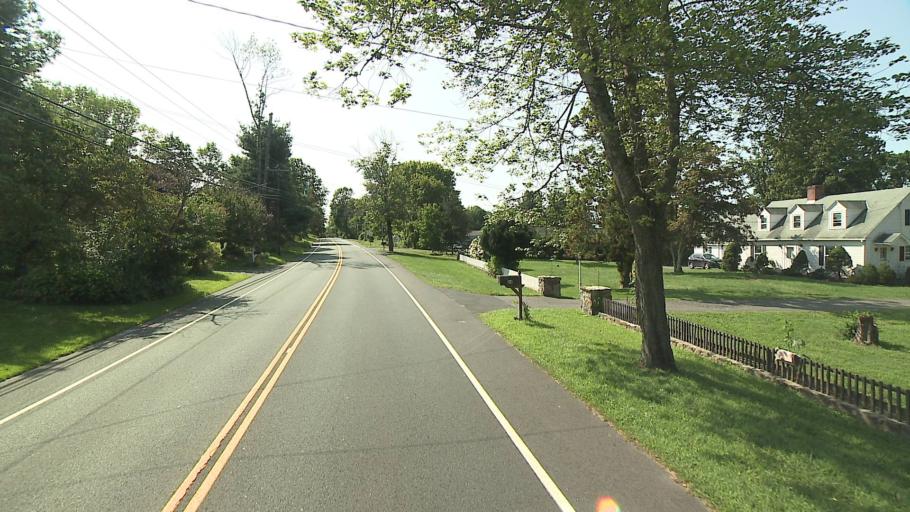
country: US
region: Connecticut
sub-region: Fairfield County
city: Newtown
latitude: 41.4473
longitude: -73.3761
